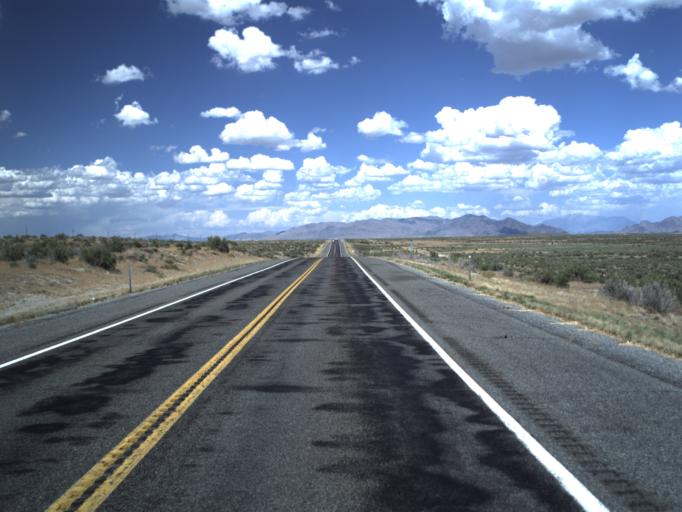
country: US
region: Utah
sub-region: Millard County
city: Delta
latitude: 39.4192
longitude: -112.4784
